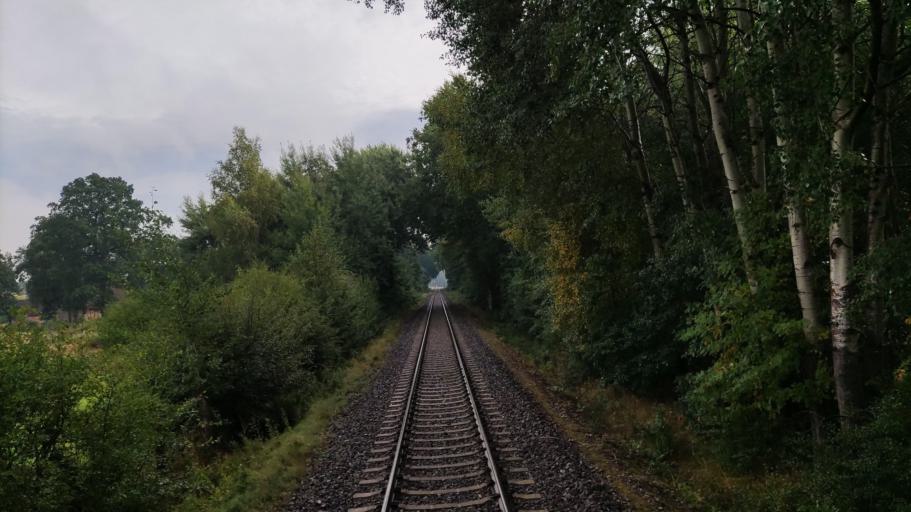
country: DE
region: Lower Saxony
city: Soltau
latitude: 52.9824
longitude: 9.8758
